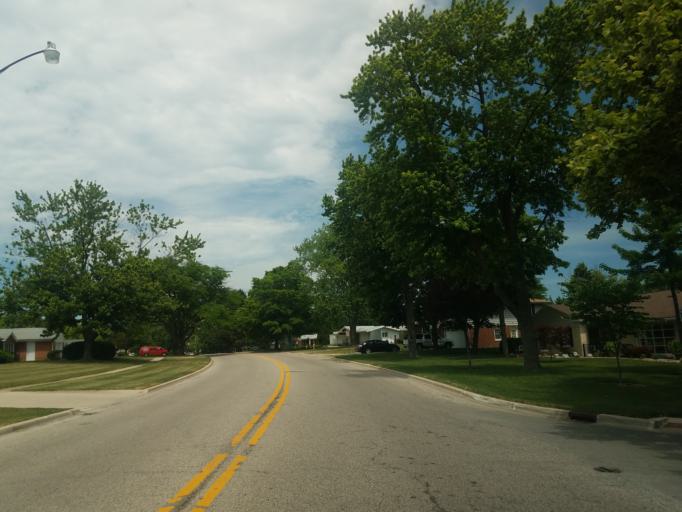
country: US
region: Illinois
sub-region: McLean County
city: Bloomington
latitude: 40.4913
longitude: -88.9616
